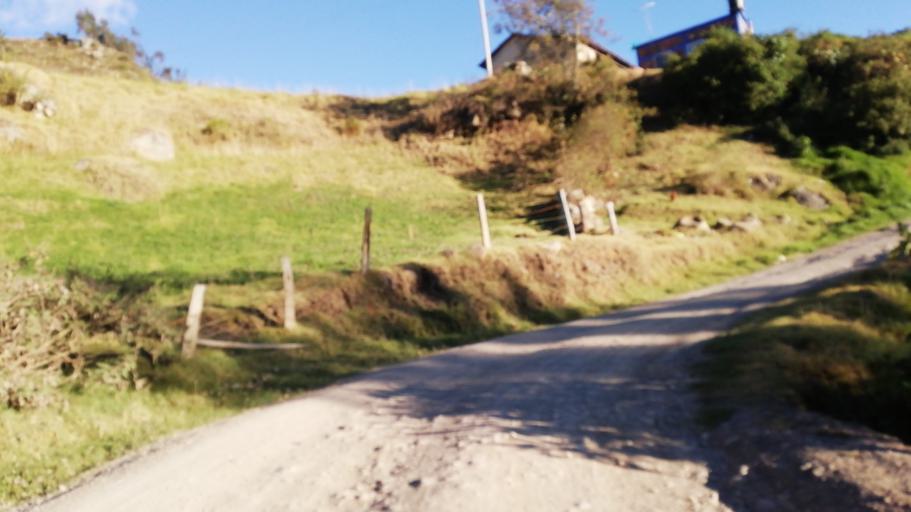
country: CO
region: Boyaca
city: Gameza
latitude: 5.7848
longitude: -72.7988
